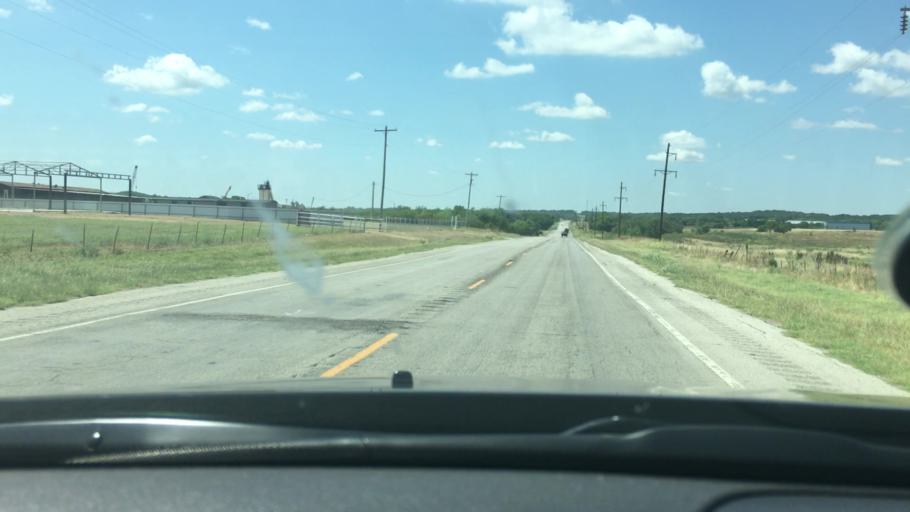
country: US
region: Oklahoma
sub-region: Carter County
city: Ardmore
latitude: 34.0838
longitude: -97.1429
